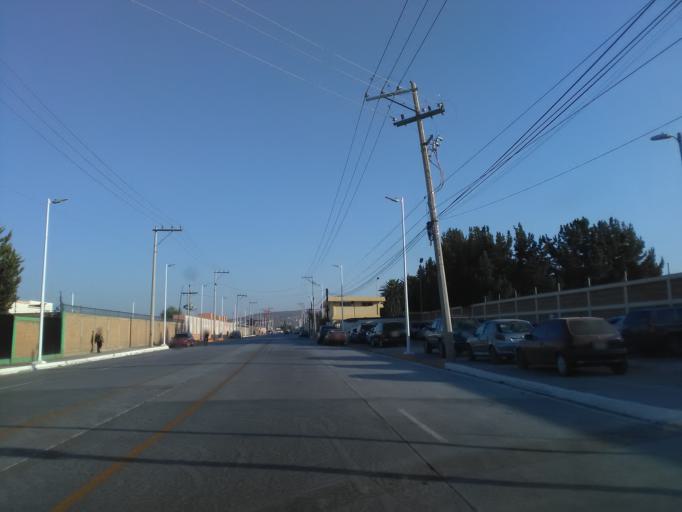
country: MX
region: Durango
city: Victoria de Durango
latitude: 24.0615
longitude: -104.6147
